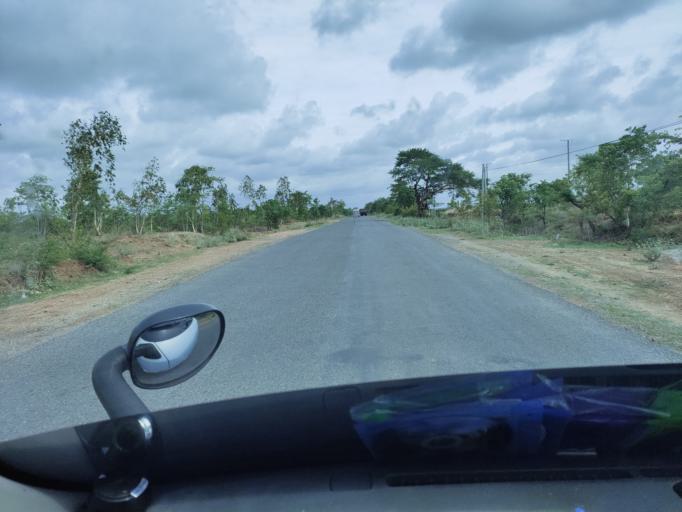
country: MM
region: Magway
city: Chauk
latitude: 20.9757
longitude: 95.0523
